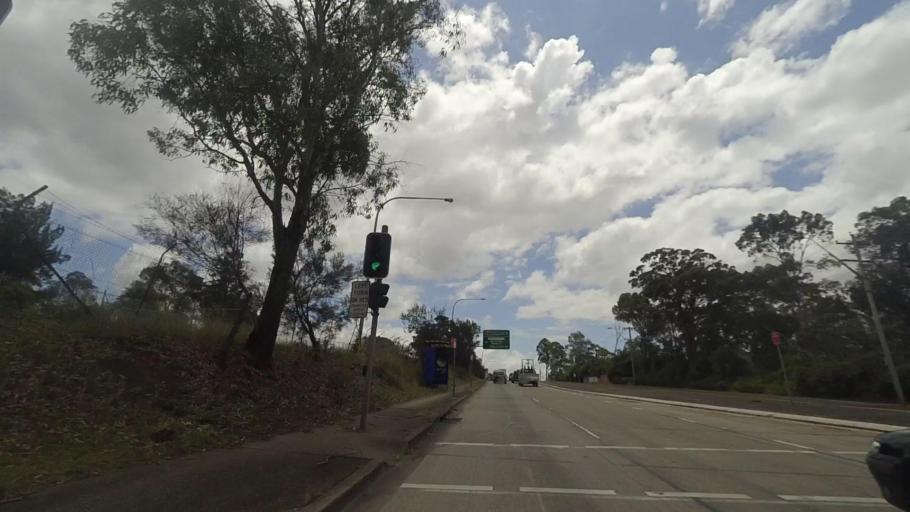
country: AU
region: New South Wales
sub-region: Fairfield
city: Cabramatta West
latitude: -33.9017
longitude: 150.9184
